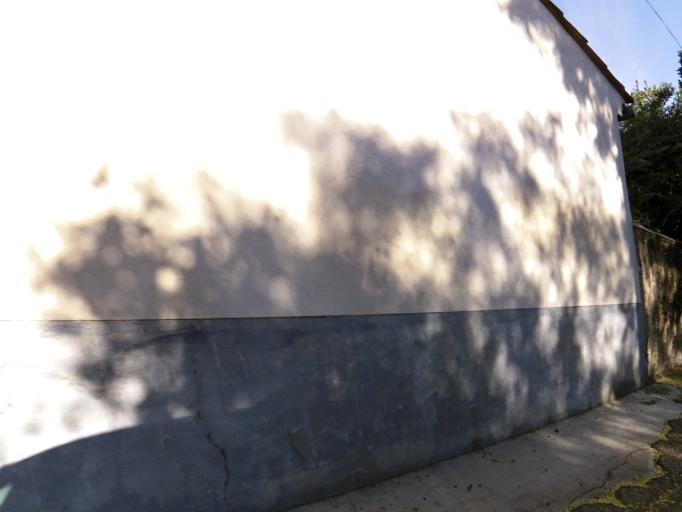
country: FR
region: Languedoc-Roussillon
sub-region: Departement du Gard
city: Nimes
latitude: 43.8540
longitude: 4.3719
